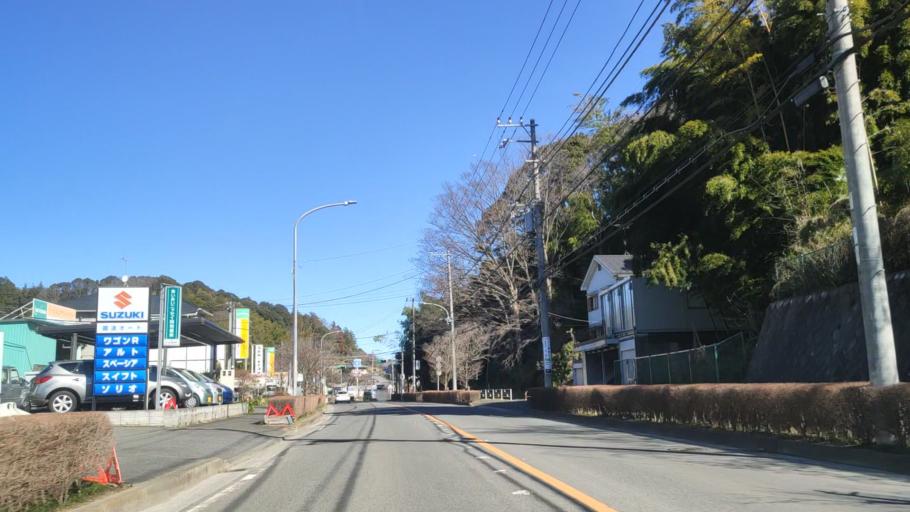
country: JP
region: Kanagawa
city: Minami-rinkan
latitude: 35.5049
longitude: 139.5161
